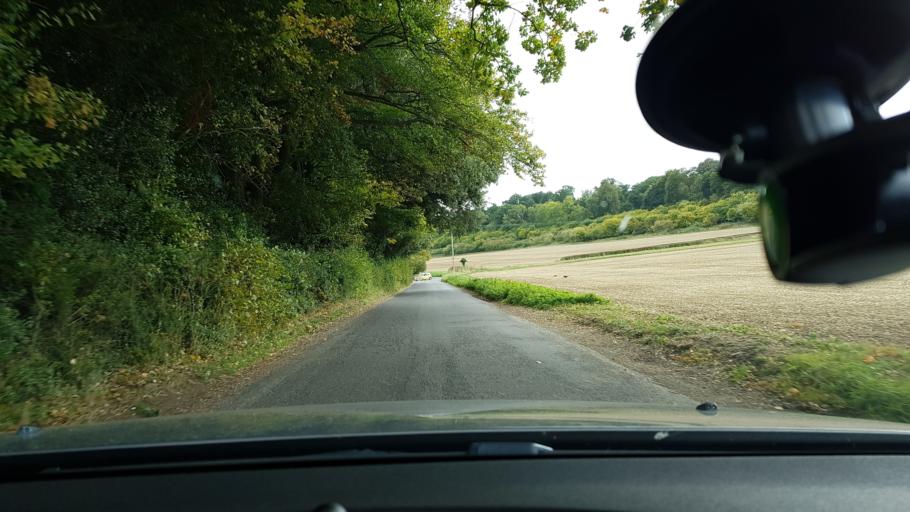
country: GB
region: England
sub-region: Wiltshire
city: Chilton Foliat
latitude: 51.4287
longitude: -1.5407
